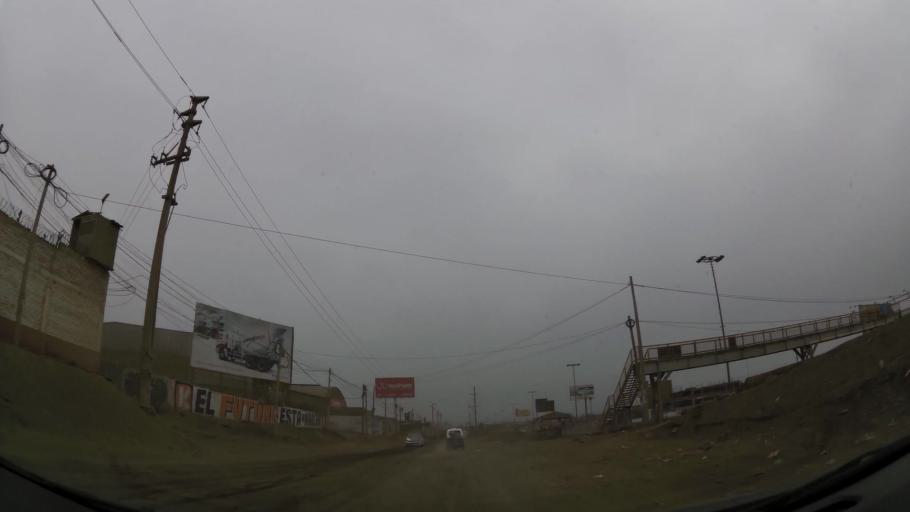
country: PE
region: Lima
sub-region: Lima
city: Surco
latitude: -12.2121
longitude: -76.9757
